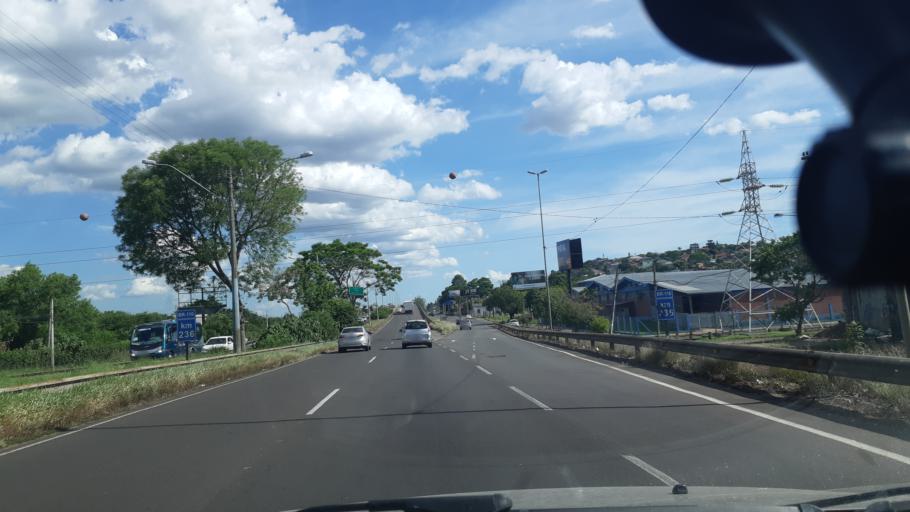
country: BR
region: Rio Grande do Sul
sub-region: Novo Hamburgo
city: Novo Hamburgo
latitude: -29.6654
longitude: -51.1436
